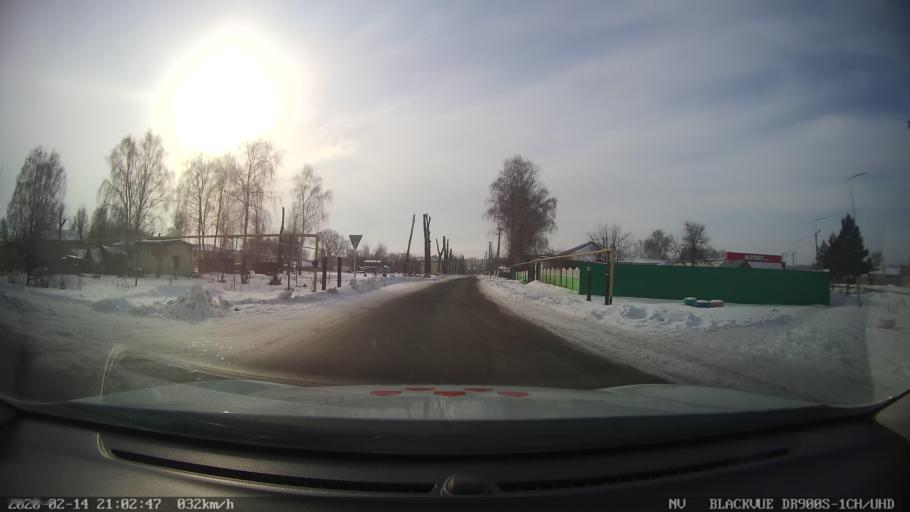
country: RU
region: Tatarstan
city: Kuybyshevskiy Zaton
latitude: 55.1593
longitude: 49.1778
